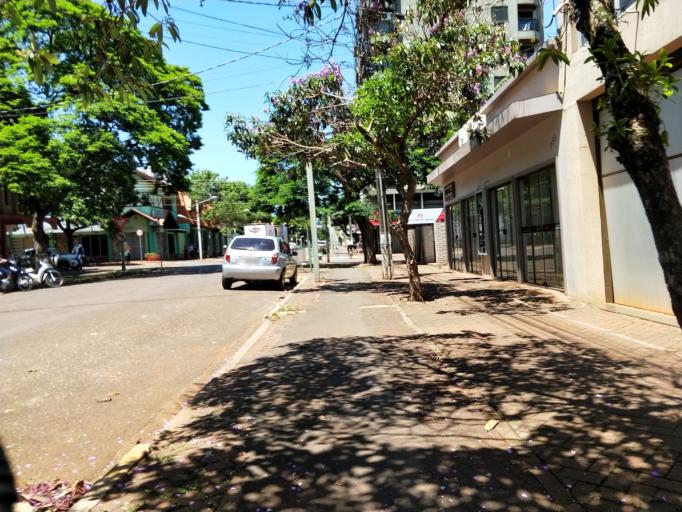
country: BR
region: Parana
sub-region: Marechal Candido Rondon
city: Marechal Candido Rondon
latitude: -24.5587
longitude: -54.0600
